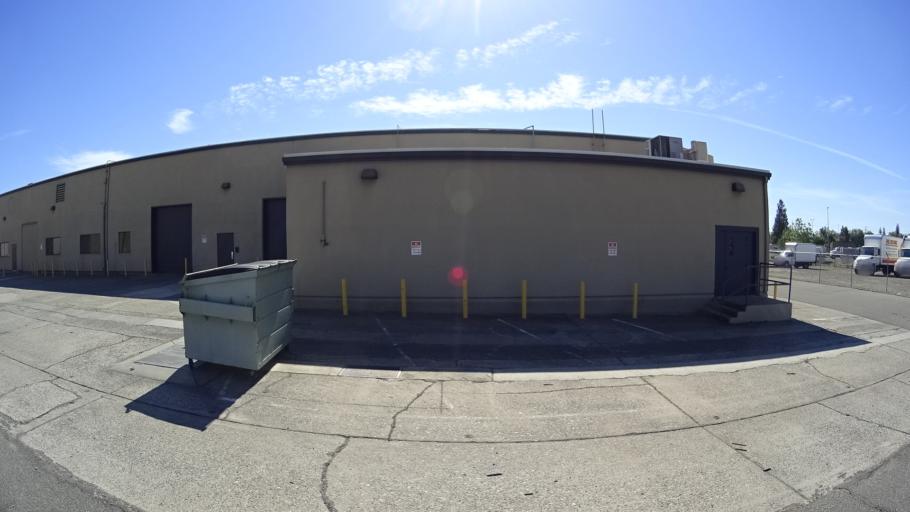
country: US
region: California
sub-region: Sacramento County
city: North Highlands
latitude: 38.6564
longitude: -121.3912
